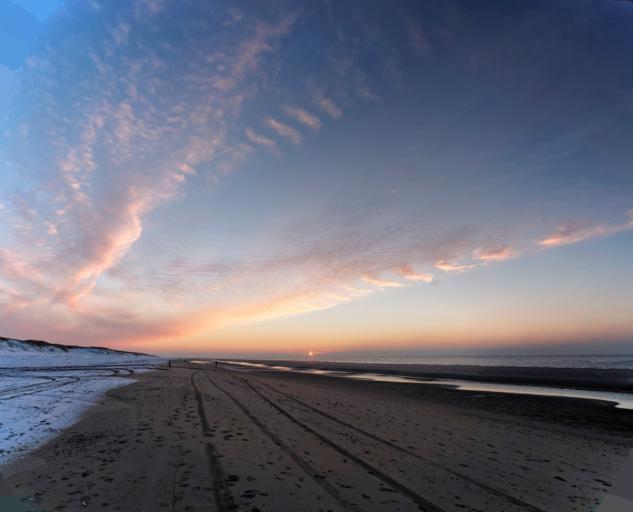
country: NL
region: North Holland
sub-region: Gemeente Texel
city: Den Burg
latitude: 53.0996
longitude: 4.7523
